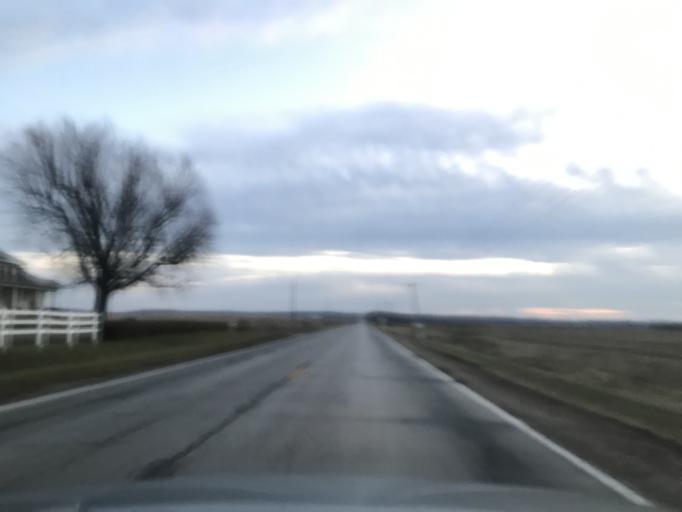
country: US
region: Iowa
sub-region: Des Moines County
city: Burlington
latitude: 40.7050
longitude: -91.0701
